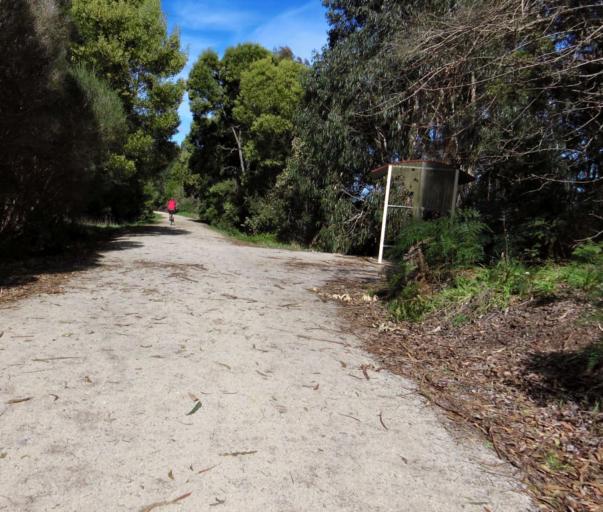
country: AU
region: Victoria
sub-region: Baw Baw
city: Warragul
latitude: -38.4898
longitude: 145.9414
